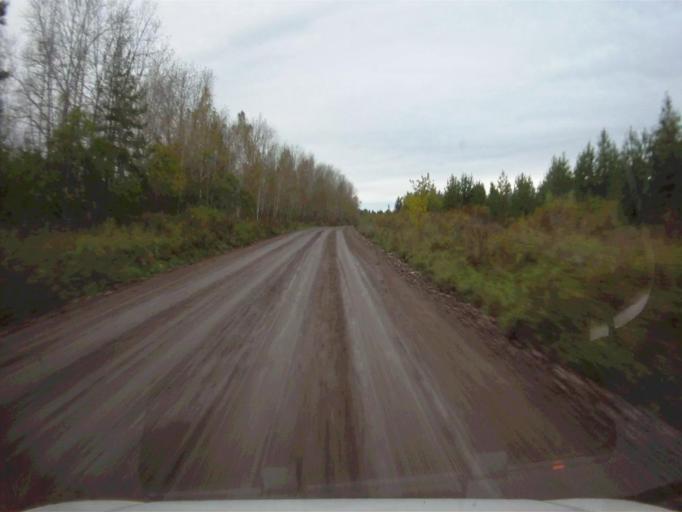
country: RU
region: Chelyabinsk
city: Nyazepetrovsk
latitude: 56.1363
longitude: 59.3020
